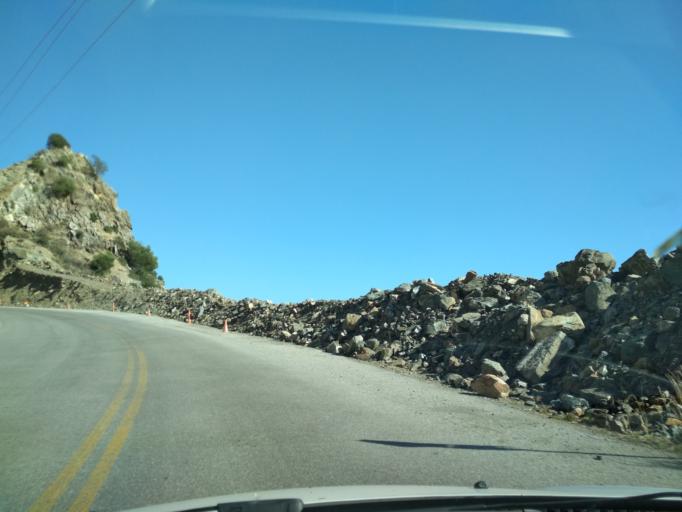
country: GR
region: Central Greece
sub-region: Nomos Evvoias
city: Roviai
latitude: 38.8470
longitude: 23.1577
